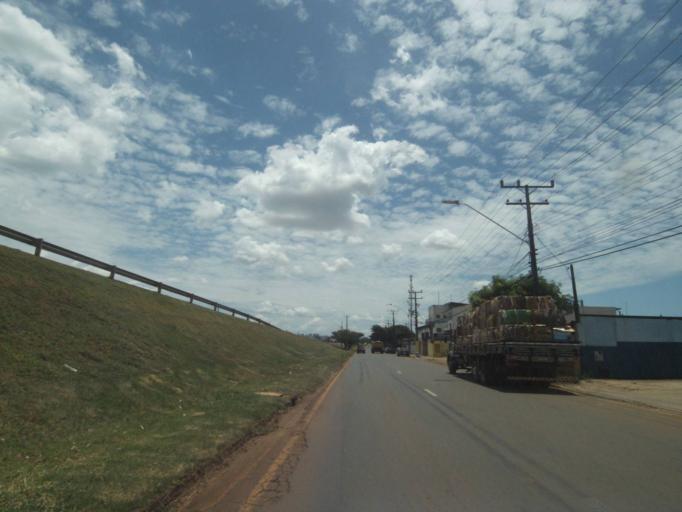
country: BR
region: Parana
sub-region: Londrina
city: Londrina
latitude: -23.3682
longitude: -51.1415
